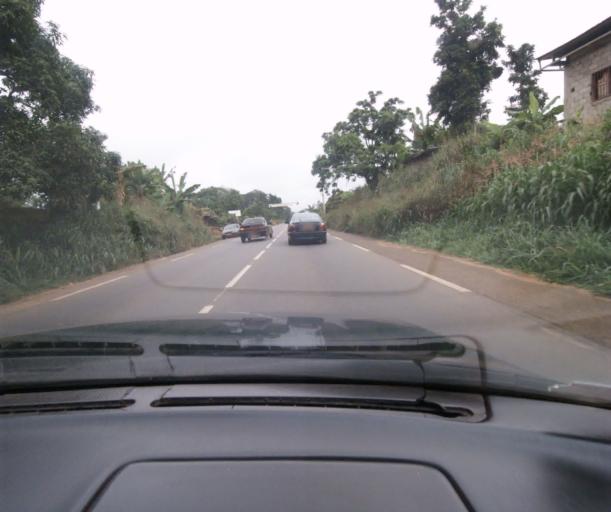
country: CM
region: Centre
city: Obala
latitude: 4.1811
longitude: 11.4689
